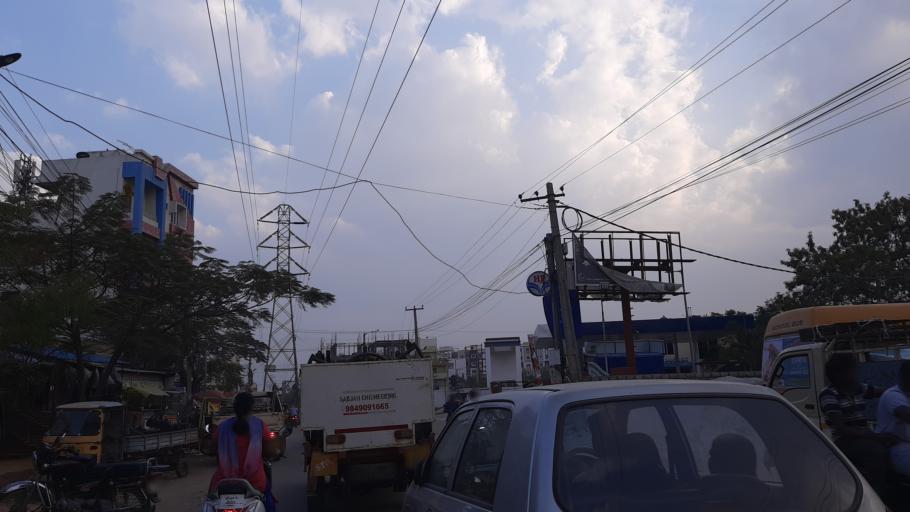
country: IN
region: Telangana
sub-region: Rangareddi
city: Kukatpalli
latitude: 17.4947
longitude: 78.4204
